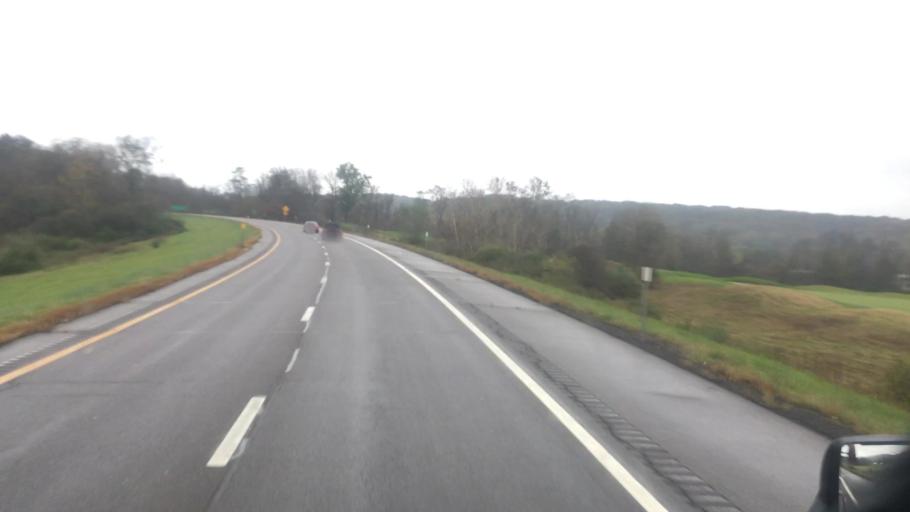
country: US
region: New York
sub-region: Tioga County
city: Apalachin
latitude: 42.0917
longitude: -76.1739
